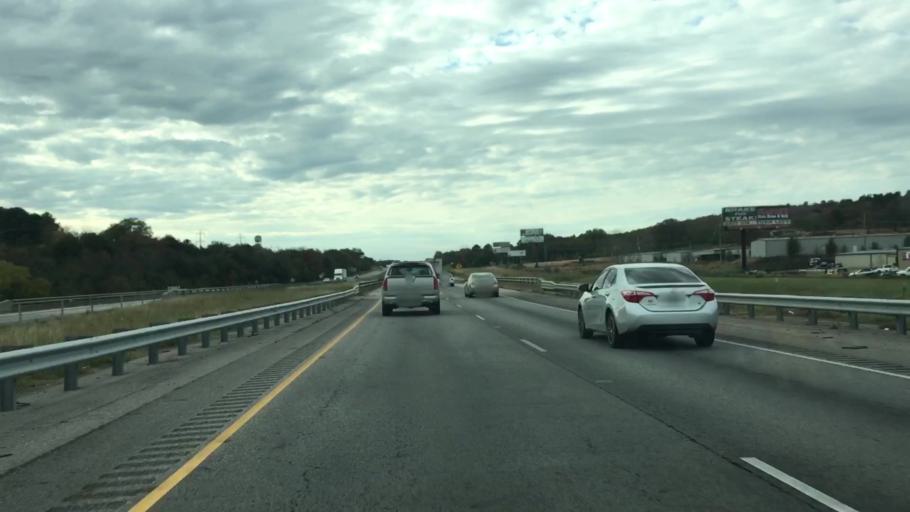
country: US
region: Arkansas
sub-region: Conway County
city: Morrilton
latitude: 35.1631
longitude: -92.6405
